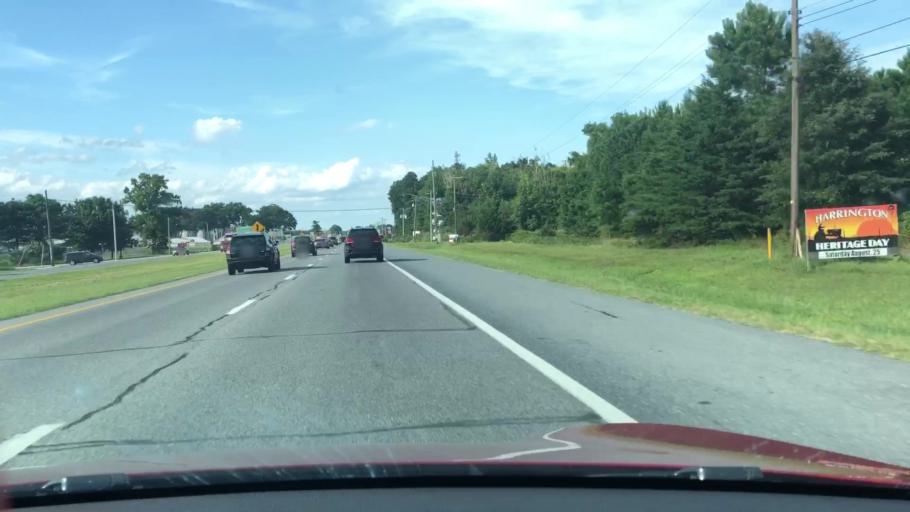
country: US
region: Delaware
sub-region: Kent County
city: Harrington
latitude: 38.9070
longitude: -75.5704
